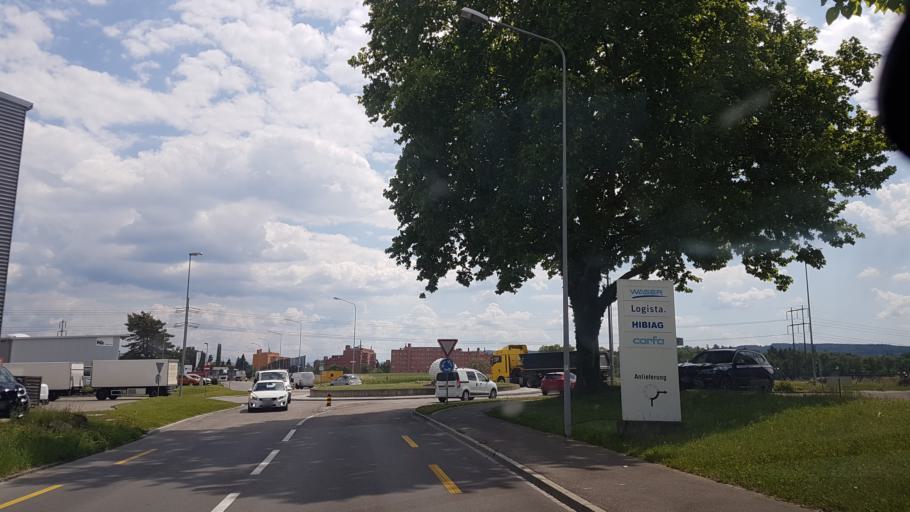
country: CH
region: Zurich
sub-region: Bezirk Uster
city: Greifensee / Muellerwis / Seilerwis
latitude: 47.3788
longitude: 8.6764
